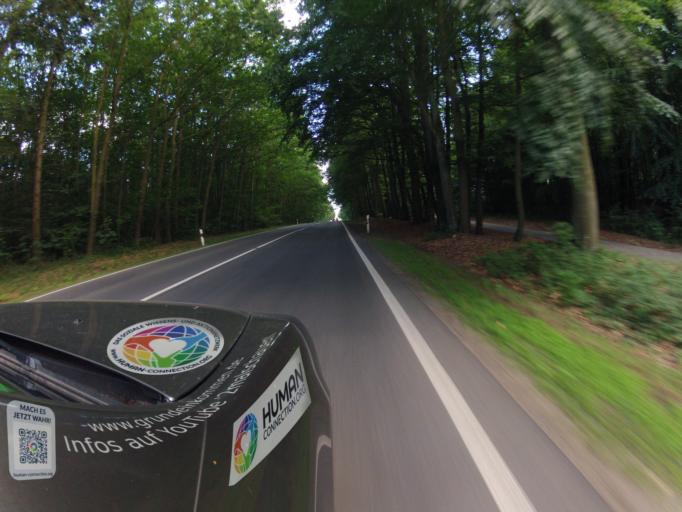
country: DE
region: Mecklenburg-Vorpommern
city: Loddin
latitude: 54.0266
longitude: 14.0334
